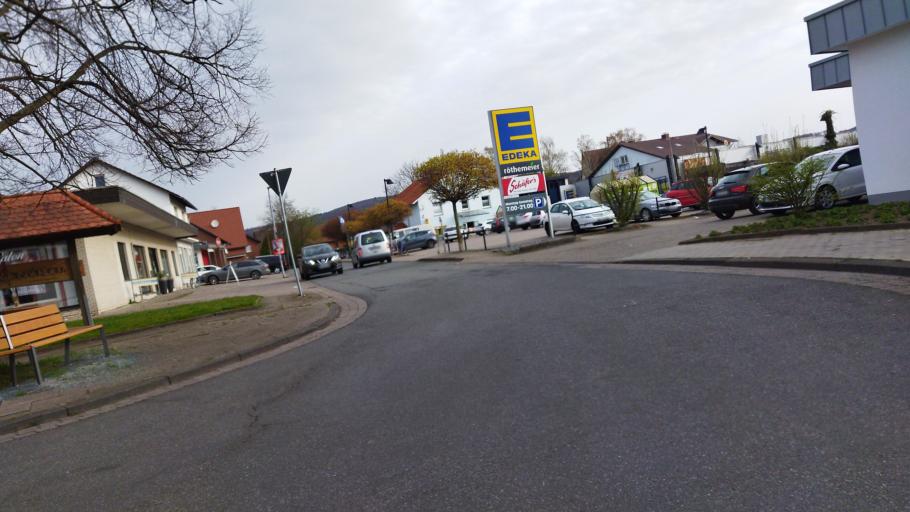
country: DE
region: Lower Saxony
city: Rinteln
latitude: 52.2018
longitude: 9.0140
